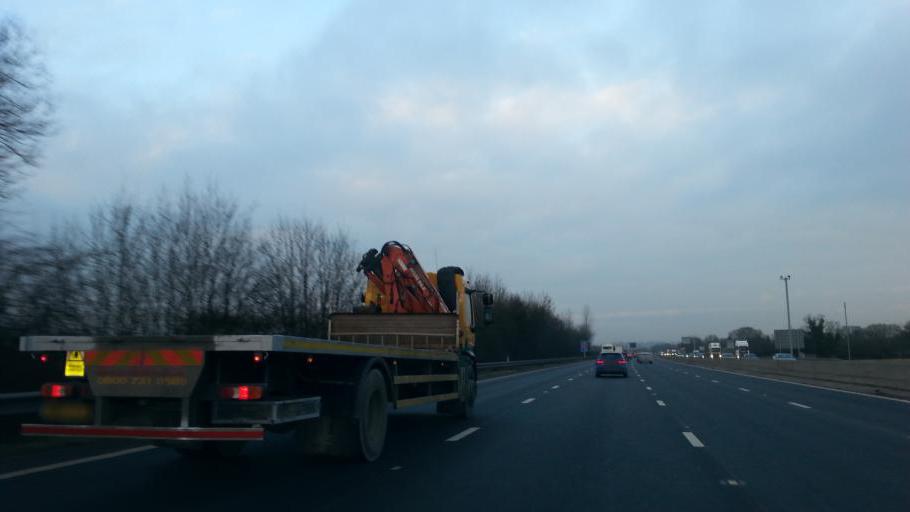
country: GB
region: England
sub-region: Worcestershire
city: Droitwich
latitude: 52.2980
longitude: -2.1165
